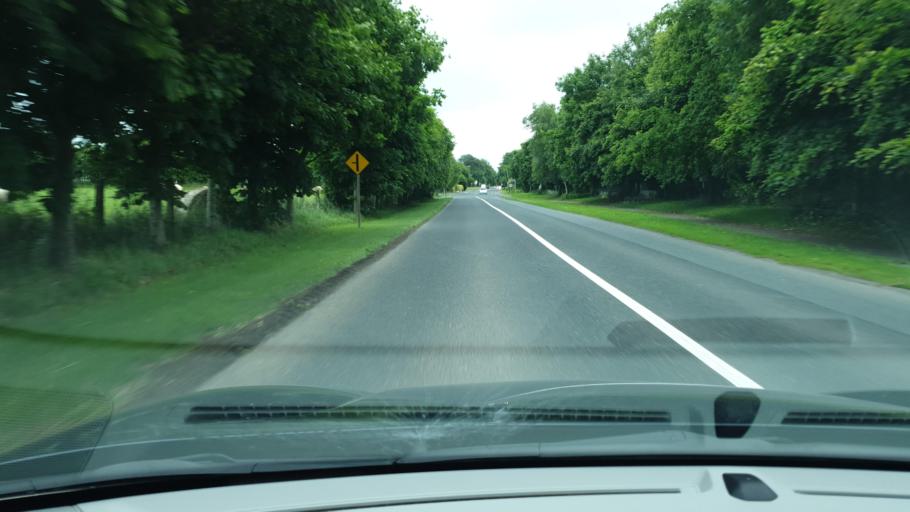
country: IE
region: Leinster
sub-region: An Mhi
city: Dunshaughlin
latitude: 53.4726
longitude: -6.5416
